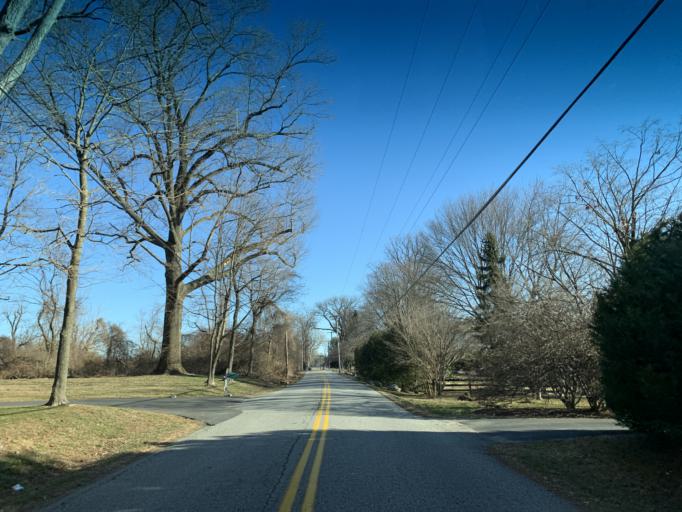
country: US
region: Maryland
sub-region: Harford County
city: Riverside
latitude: 39.5674
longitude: -76.2402
